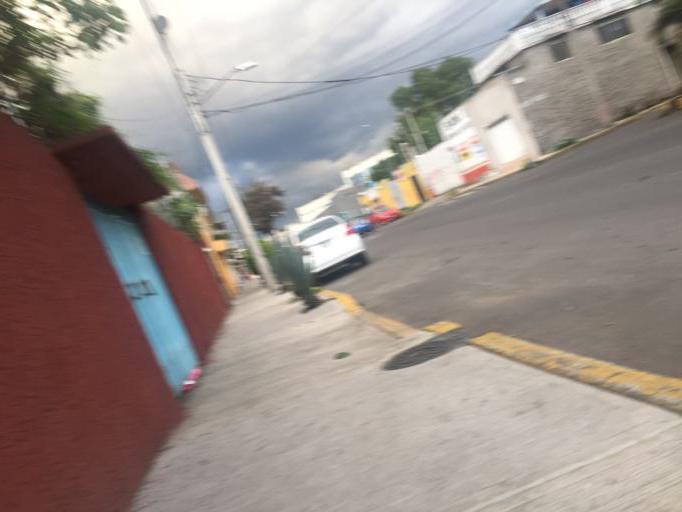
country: MX
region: Mexico City
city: Iztapalapa
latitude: 19.3517
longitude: -99.0800
